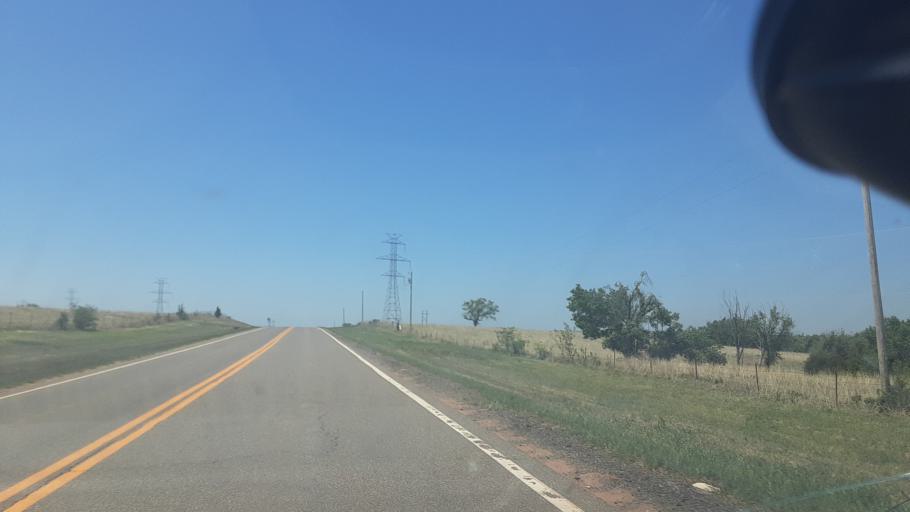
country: US
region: Oklahoma
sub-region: Noble County
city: Perry
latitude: 36.1148
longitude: -97.3728
